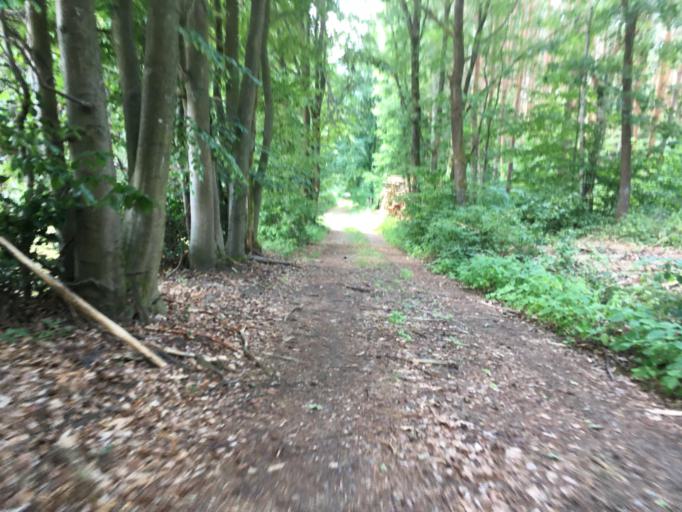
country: DE
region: Brandenburg
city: Althuttendorf
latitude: 52.9526
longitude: 13.7800
